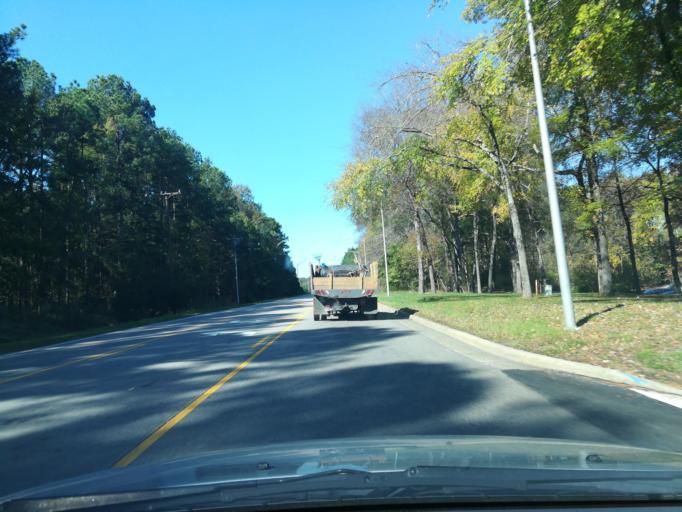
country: US
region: North Carolina
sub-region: Durham County
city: Durham
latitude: 36.0256
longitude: -78.9576
